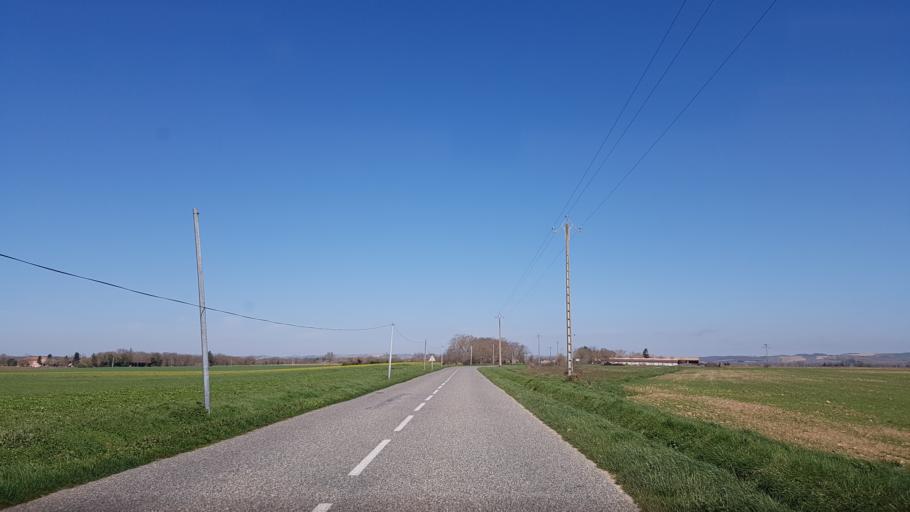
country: FR
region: Languedoc-Roussillon
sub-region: Departement de l'Aude
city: Belpech
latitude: 43.1726
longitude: 1.7099
